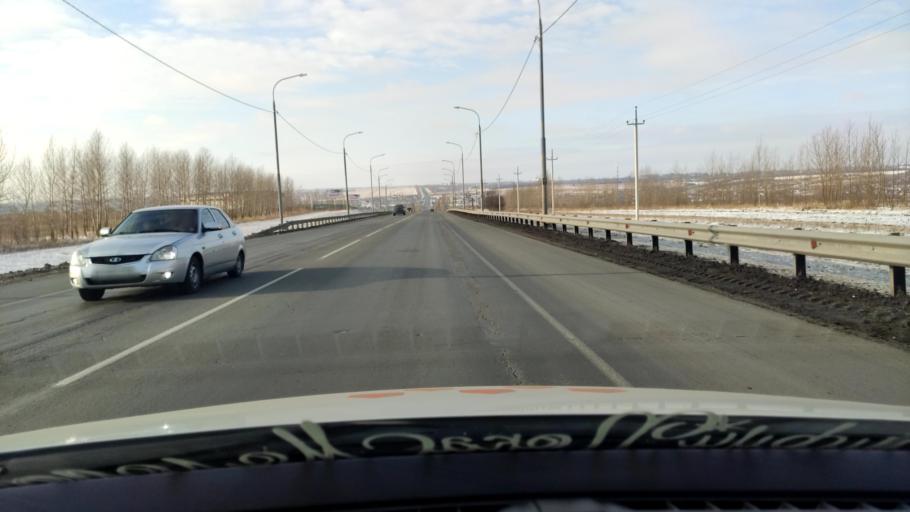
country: RU
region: Voronezj
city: Devitsa
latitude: 51.6332
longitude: 38.9666
